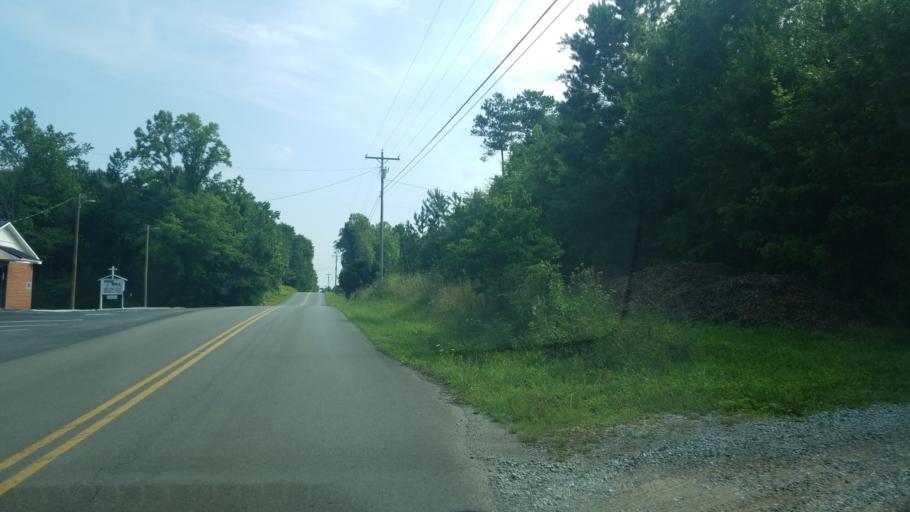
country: US
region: Tennessee
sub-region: Hamilton County
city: Apison
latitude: 35.0730
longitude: -84.9772
